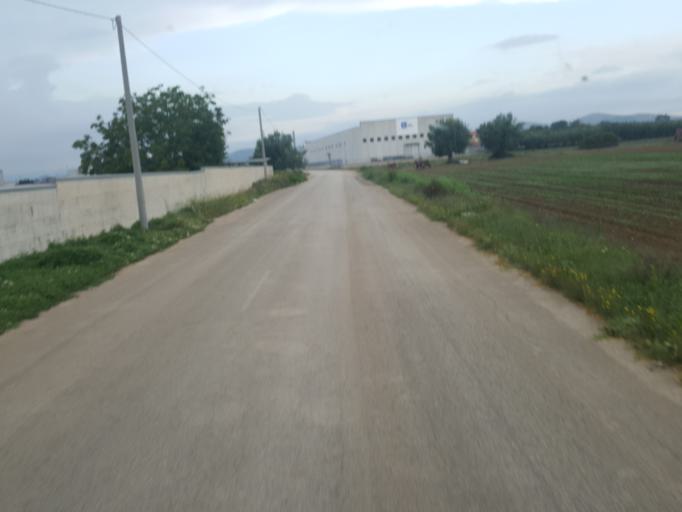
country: IT
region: Campania
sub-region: Provincia di Caserta
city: Pignataro Maggiore
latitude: 41.1742
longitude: 14.1479
